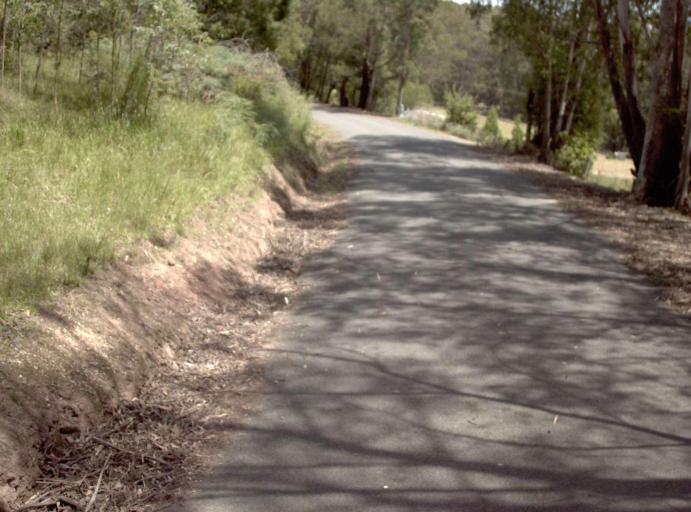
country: AU
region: New South Wales
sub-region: Bombala
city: Bombala
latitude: -37.4273
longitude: 149.0067
